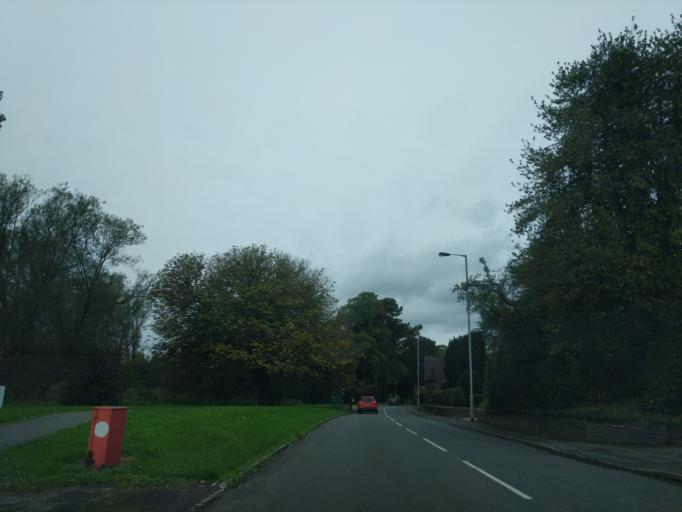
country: GB
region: England
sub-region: Staffordshire
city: Audley
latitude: 52.9980
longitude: -2.3394
